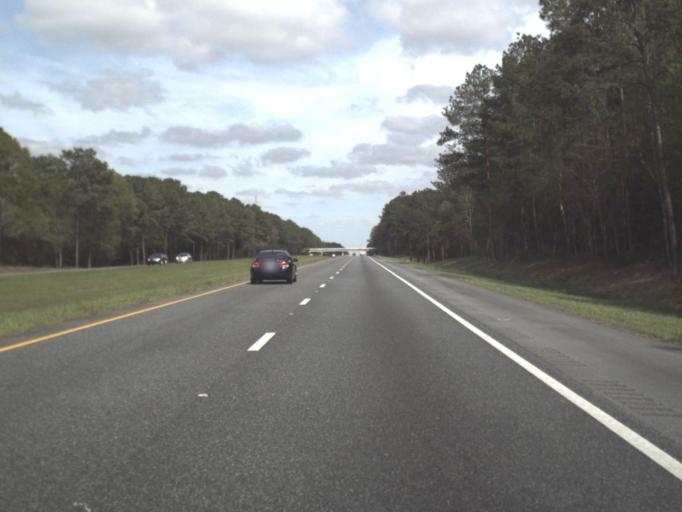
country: US
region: Florida
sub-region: Walton County
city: DeFuniak Springs
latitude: 30.6910
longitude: -86.0815
